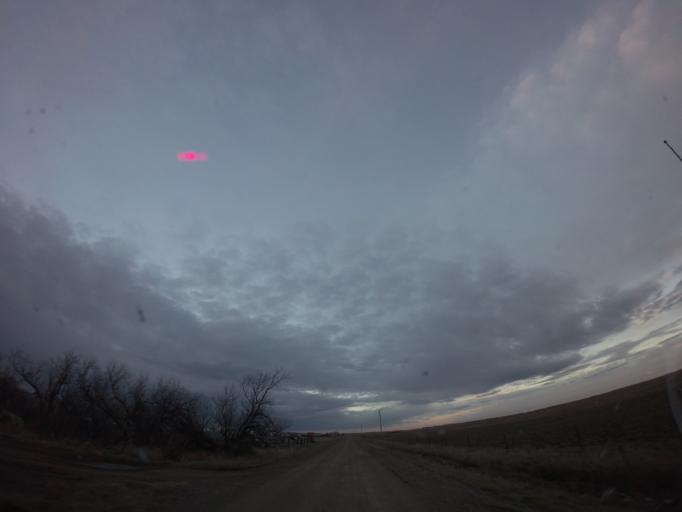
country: US
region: Montana
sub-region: Yellowstone County
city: Laurel
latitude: 45.9436
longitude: -108.7422
